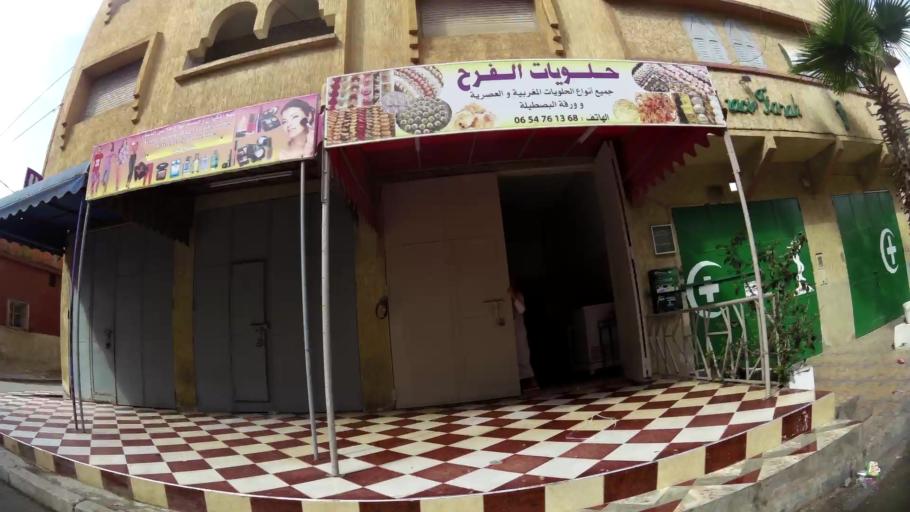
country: MA
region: Rabat-Sale-Zemmour-Zaer
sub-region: Khemisset
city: Tiflet
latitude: 33.8942
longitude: -6.3149
